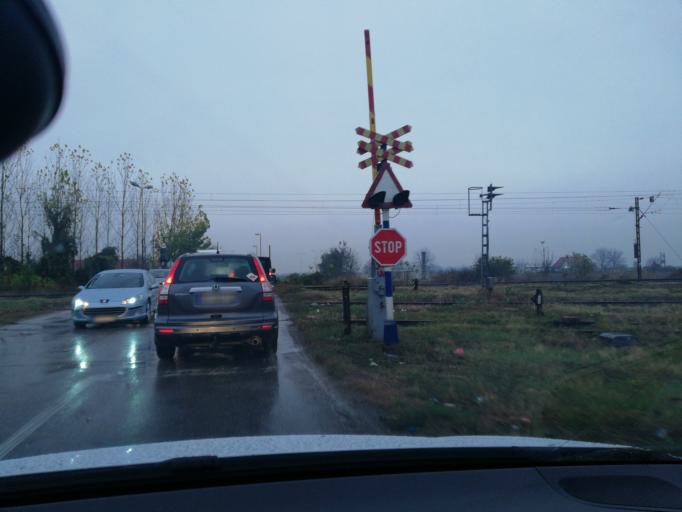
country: RS
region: Autonomna Pokrajina Vojvodina
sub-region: Sremski Okrug
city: Ruma
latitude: 44.9897
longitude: 19.8163
